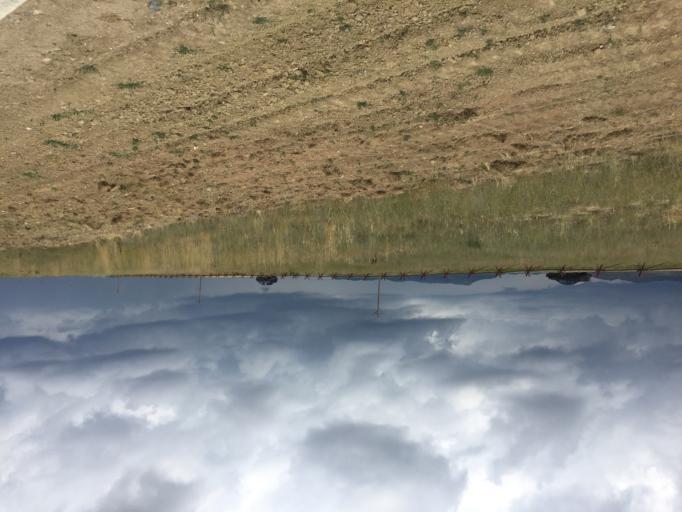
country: US
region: Colorado
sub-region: Larimer County
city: Loveland
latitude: 40.4705
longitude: -105.0958
